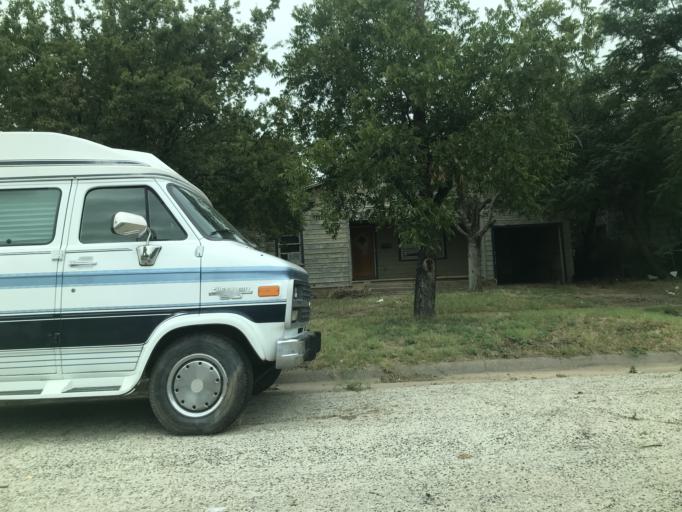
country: US
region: Texas
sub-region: Taylor County
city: Abilene
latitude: 32.4400
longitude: -99.7358
